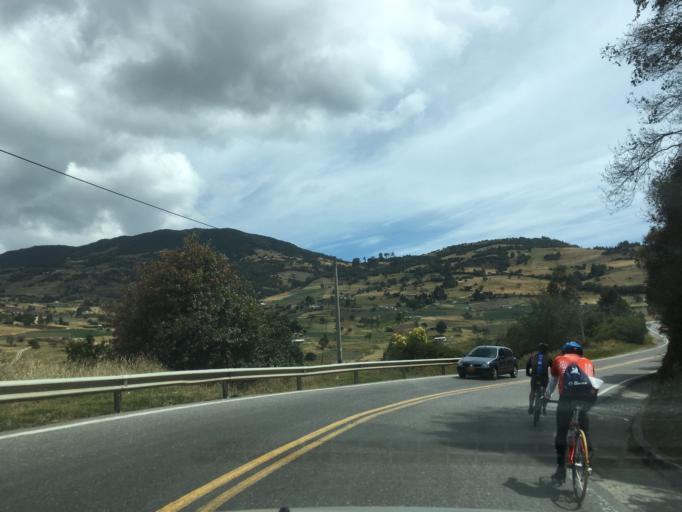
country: CO
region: Boyaca
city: Firavitoba
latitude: 5.6213
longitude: -72.9097
